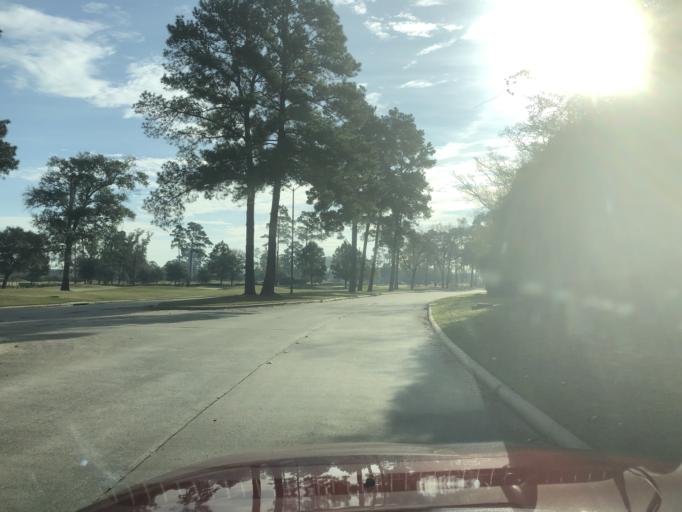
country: US
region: Texas
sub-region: Harris County
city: Spring
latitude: 30.0040
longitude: -95.4744
